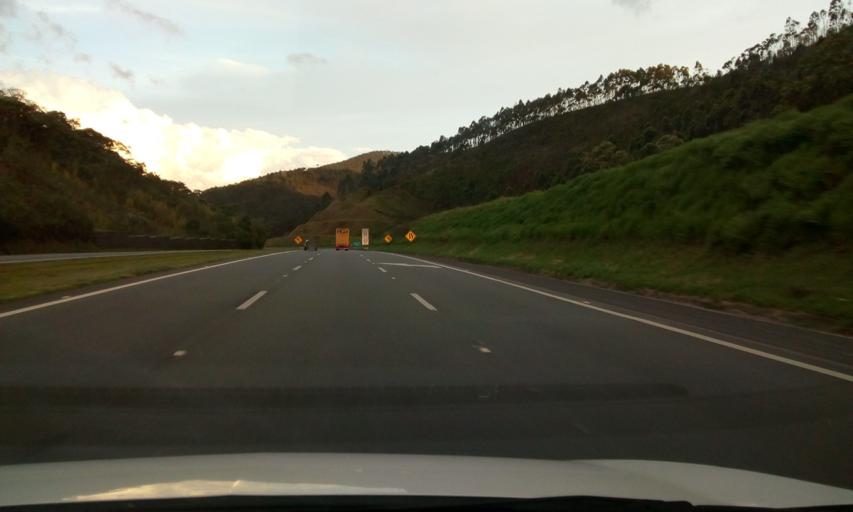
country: BR
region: Sao Paulo
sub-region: Santa Isabel
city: Santa Isabel
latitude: -23.1740
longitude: -46.2589
